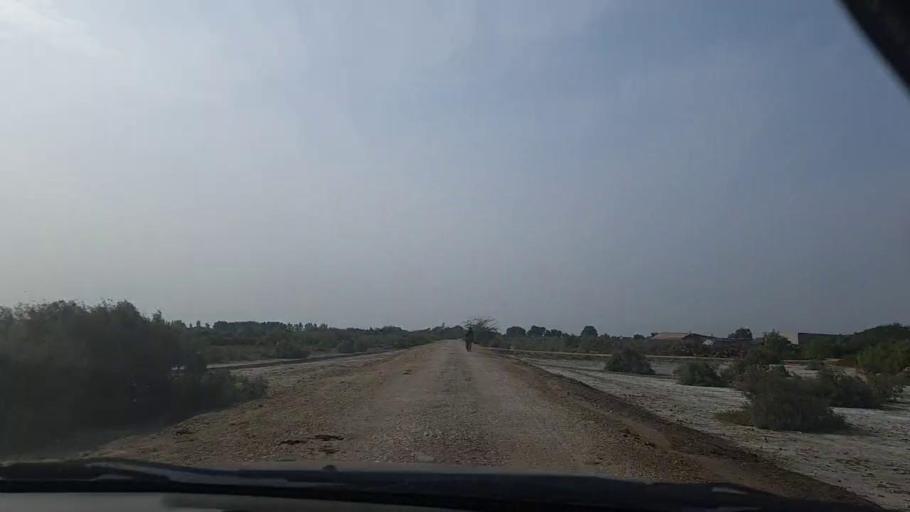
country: PK
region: Sindh
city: Thatta
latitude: 24.6136
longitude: 67.9512
